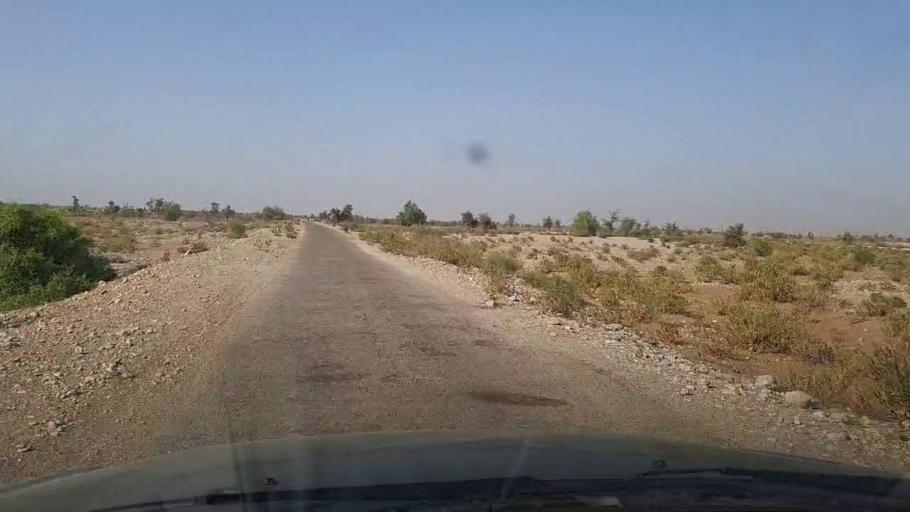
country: PK
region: Sindh
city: Sann
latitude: 25.9272
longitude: 68.0193
